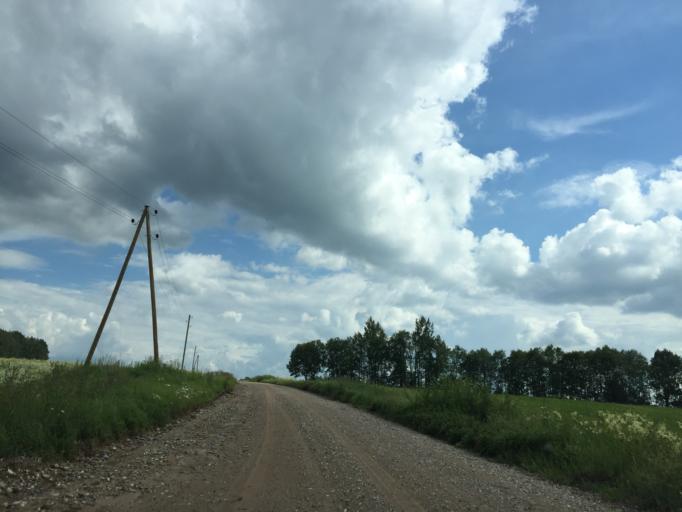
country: LV
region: Ligatne
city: Ligatne
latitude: 57.2172
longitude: 24.9475
